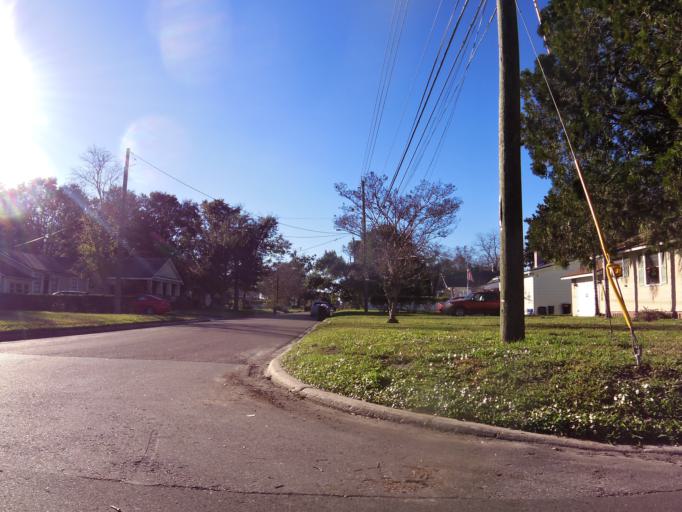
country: US
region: Florida
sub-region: Duval County
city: Jacksonville
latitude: 30.2832
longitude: -81.7178
